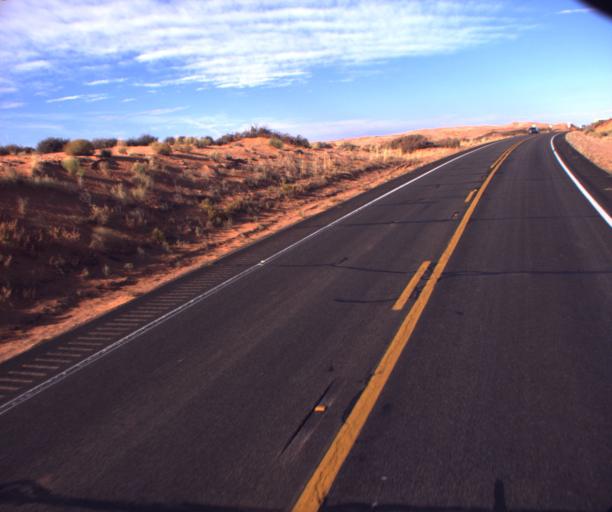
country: US
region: Arizona
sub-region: Apache County
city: Many Farms
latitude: 36.9240
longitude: -109.6096
